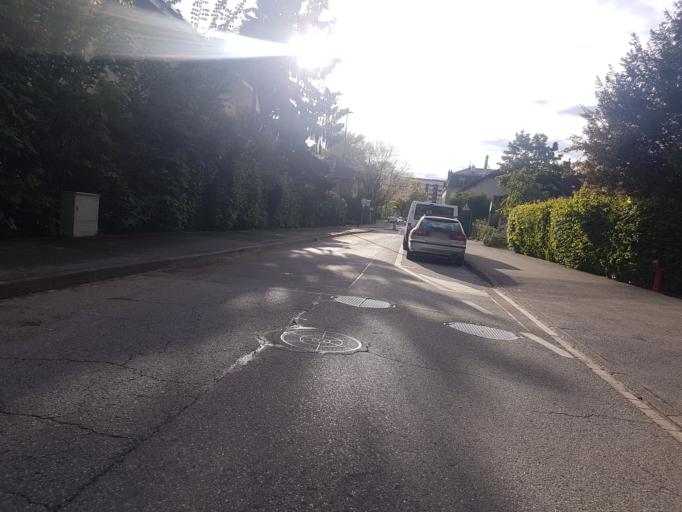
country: CH
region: Geneva
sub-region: Geneva
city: Lancy
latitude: 46.2055
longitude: 6.1131
